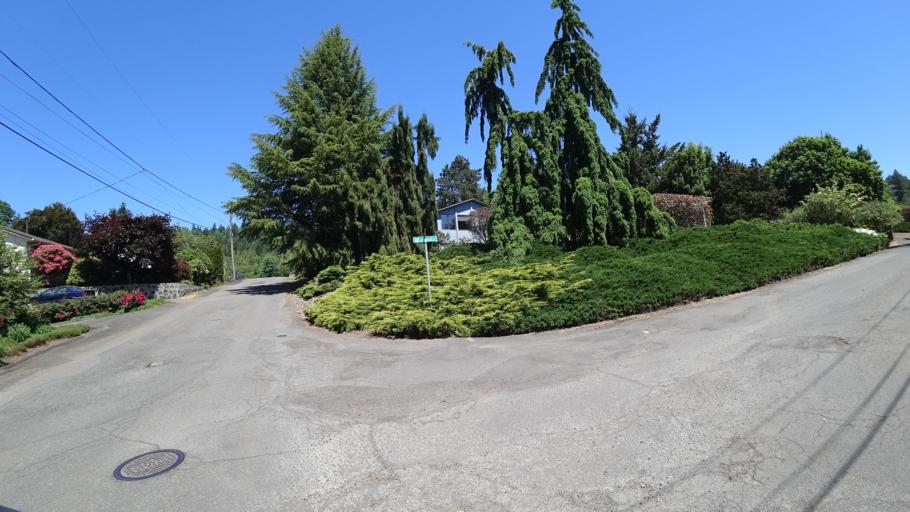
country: US
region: Oregon
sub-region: Washington County
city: Raleigh Hills
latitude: 45.4941
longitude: -122.7199
